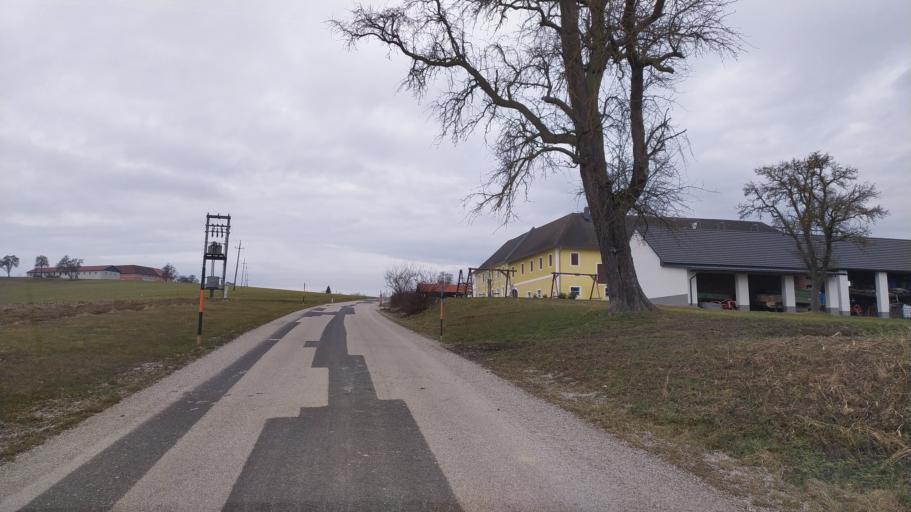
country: AT
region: Lower Austria
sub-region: Politischer Bezirk Amstetten
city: Zeillern
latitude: 48.1325
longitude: 14.7194
